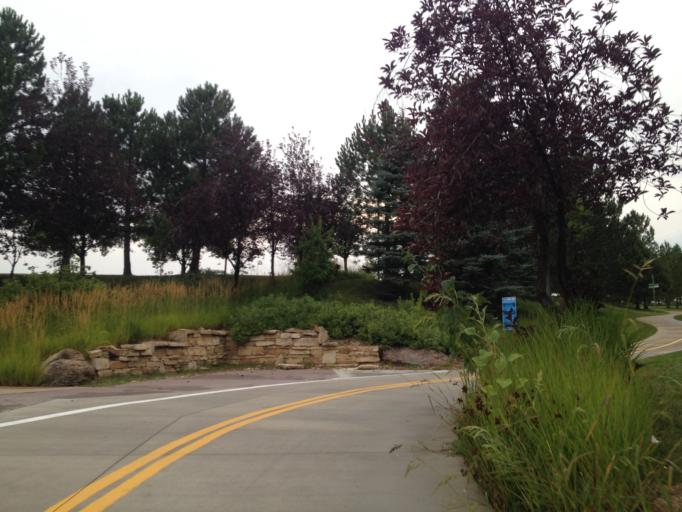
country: US
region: Colorado
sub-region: Broomfield County
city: Broomfield
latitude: 39.9331
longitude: -105.1282
